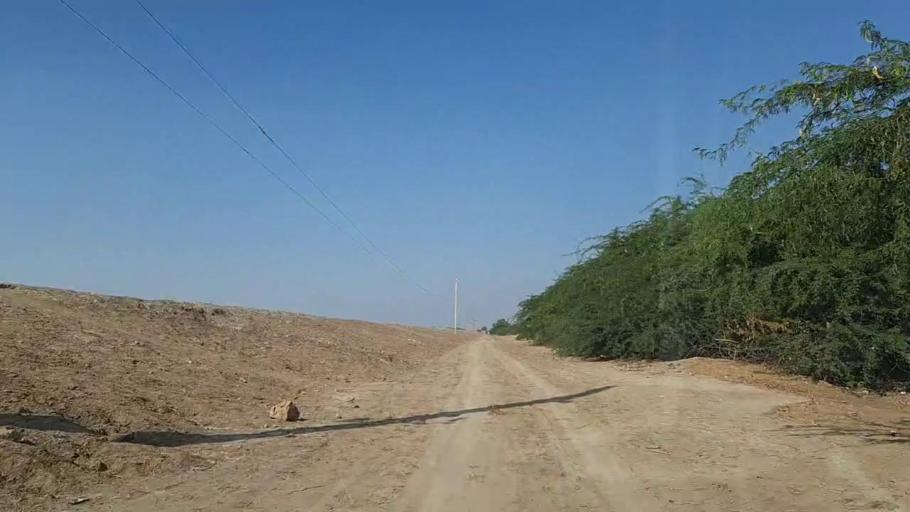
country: PK
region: Sindh
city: Chuhar Jamali
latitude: 24.5403
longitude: 68.0158
